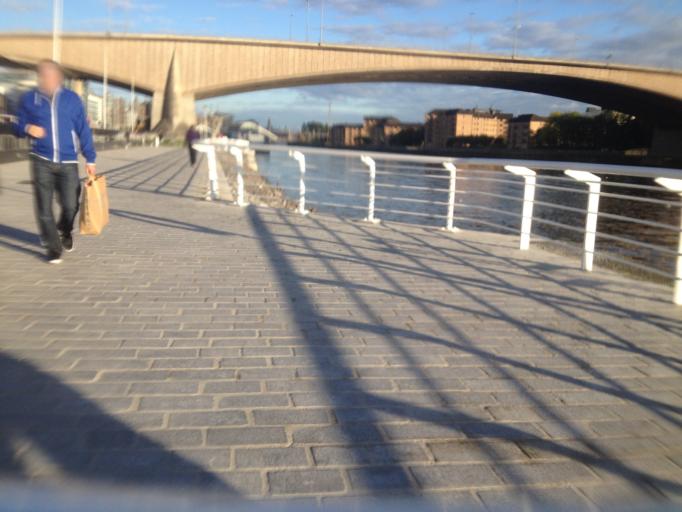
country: GB
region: Scotland
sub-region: Glasgow City
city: Glasgow
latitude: 55.8565
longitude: -4.2726
